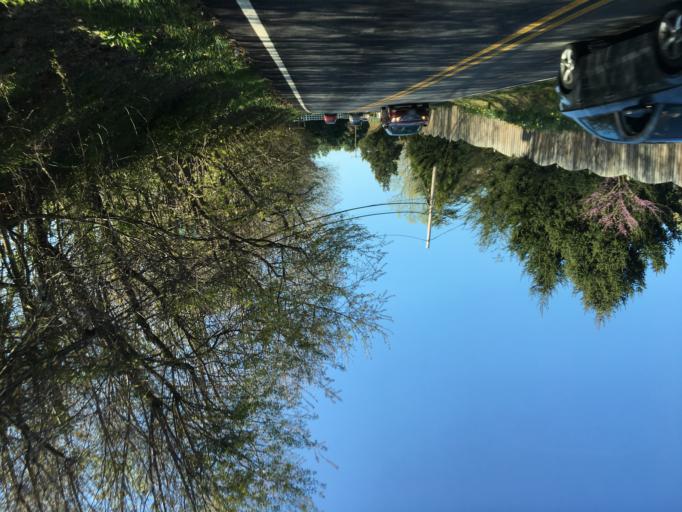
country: US
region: Maryland
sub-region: Baltimore County
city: Hampton
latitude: 39.5015
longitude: -76.5301
